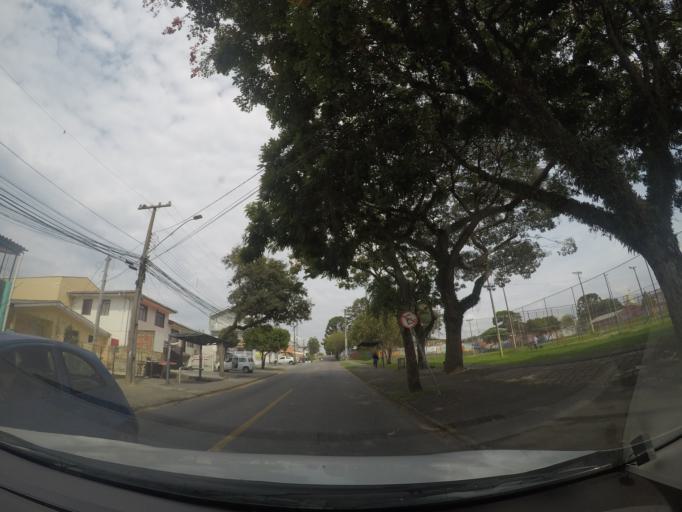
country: BR
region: Parana
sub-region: Sao Jose Dos Pinhais
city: Sao Jose dos Pinhais
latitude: -25.5160
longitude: -49.2753
